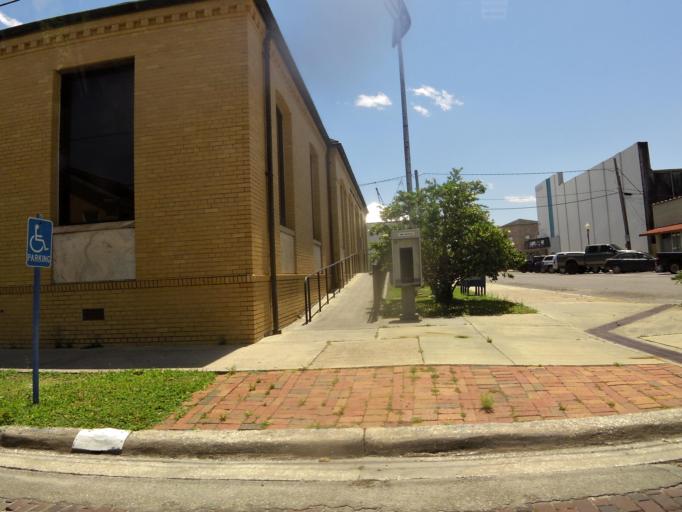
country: US
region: Florida
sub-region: Bradford County
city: Starke
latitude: 29.9448
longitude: -82.1094
